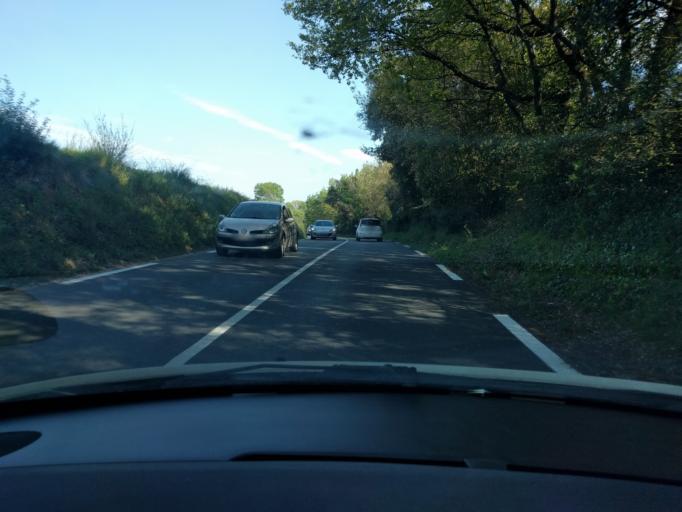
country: FR
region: Provence-Alpes-Cote d'Azur
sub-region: Departement du Var
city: Hyeres
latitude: 43.1523
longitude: 6.1301
